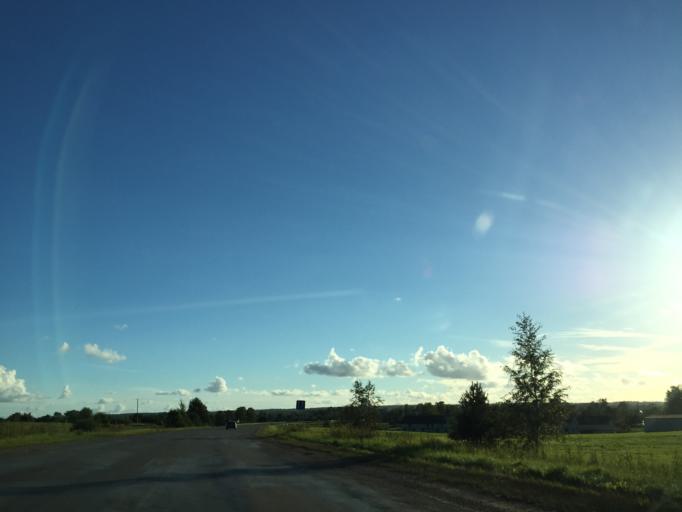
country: LV
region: Kuldigas Rajons
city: Kuldiga
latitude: 56.9654
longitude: 22.0111
